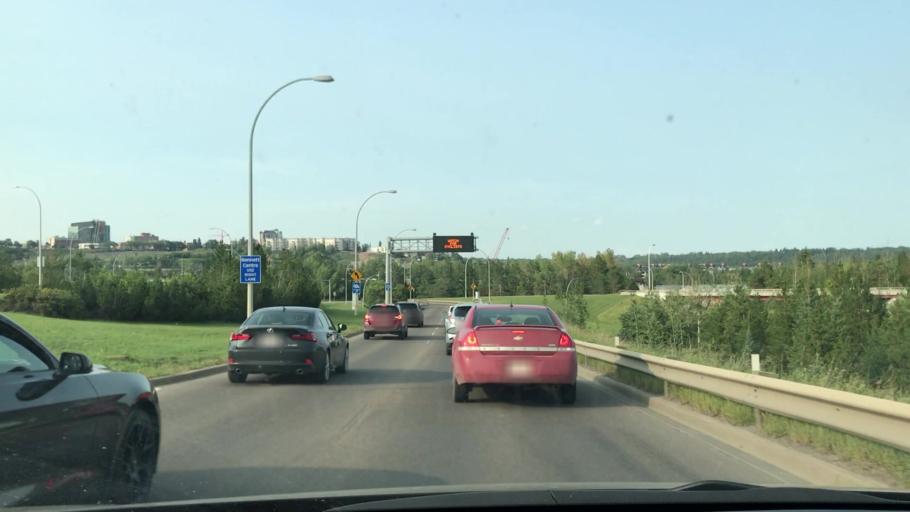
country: CA
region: Alberta
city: Edmonton
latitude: 53.5329
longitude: -113.4846
